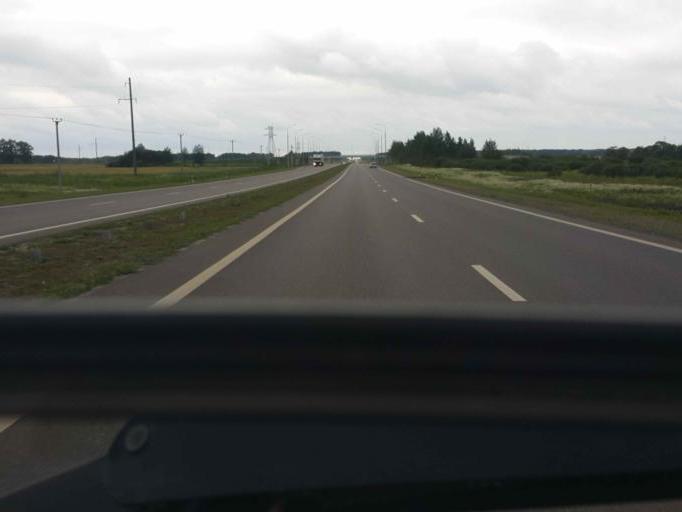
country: RU
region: Tambov
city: Zavoronezhskoye
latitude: 52.8849
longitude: 40.7201
